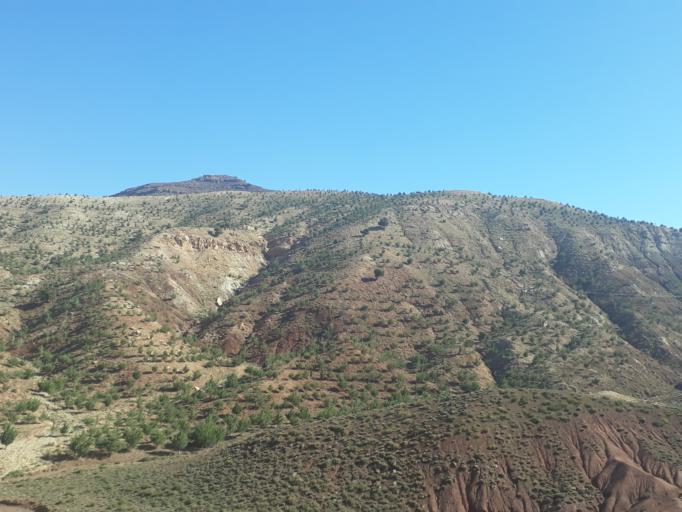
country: MA
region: Souss-Massa-Draa
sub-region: Ouarzazate
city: Telouet
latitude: 31.2615
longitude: -7.3939
